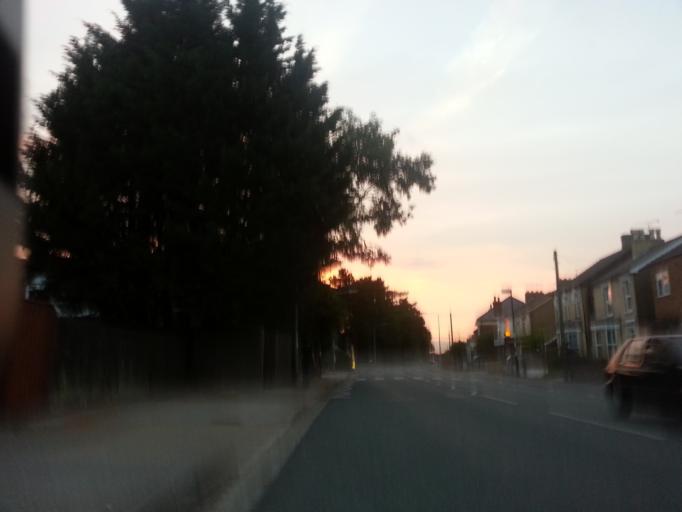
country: GB
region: England
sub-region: Suffolk
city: Ipswich
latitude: 52.0446
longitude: 1.1804
